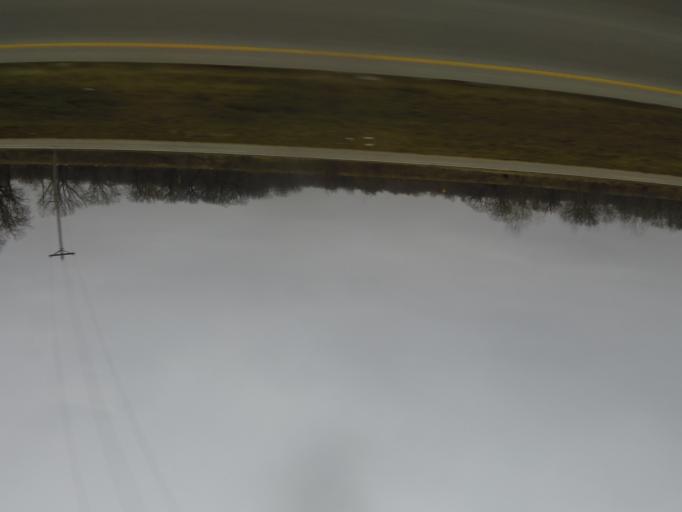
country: US
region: Missouri
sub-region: Lewis County
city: Canton
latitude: 40.1741
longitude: -91.5264
